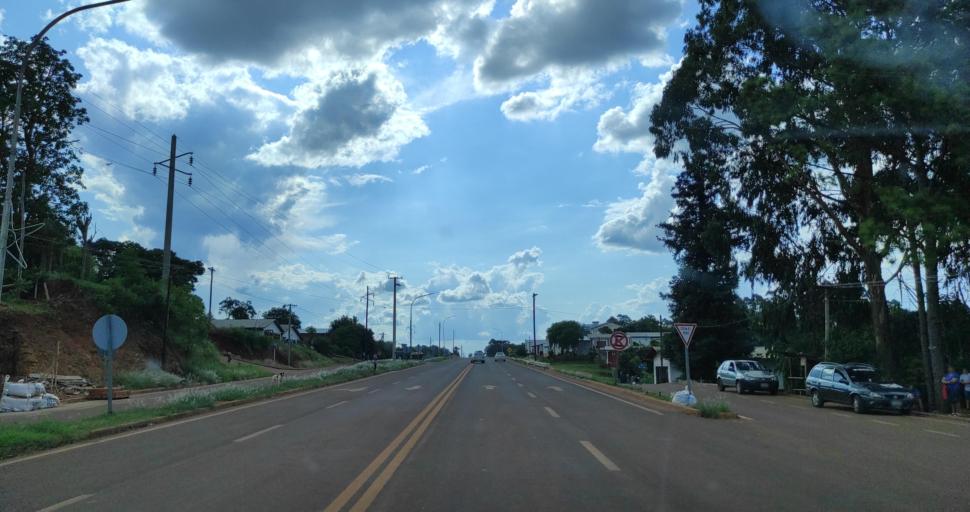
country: AR
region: Misiones
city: Bernardo de Irigoyen
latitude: -26.2941
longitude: -53.7588
